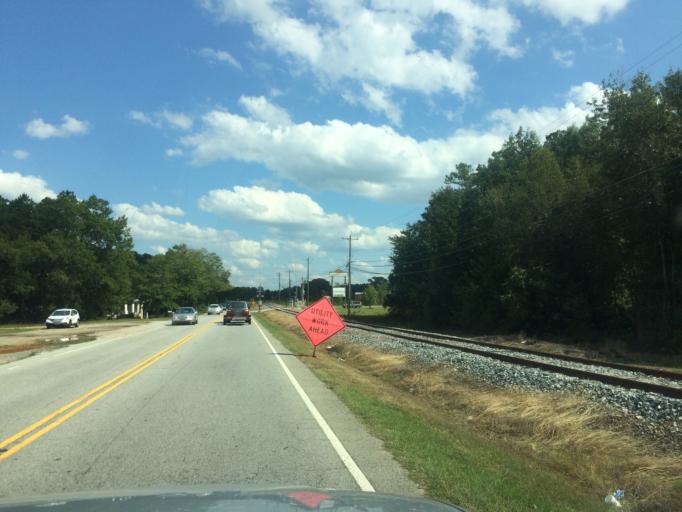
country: US
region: South Carolina
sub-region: Anderson County
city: Belton
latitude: 34.5150
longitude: -82.4824
